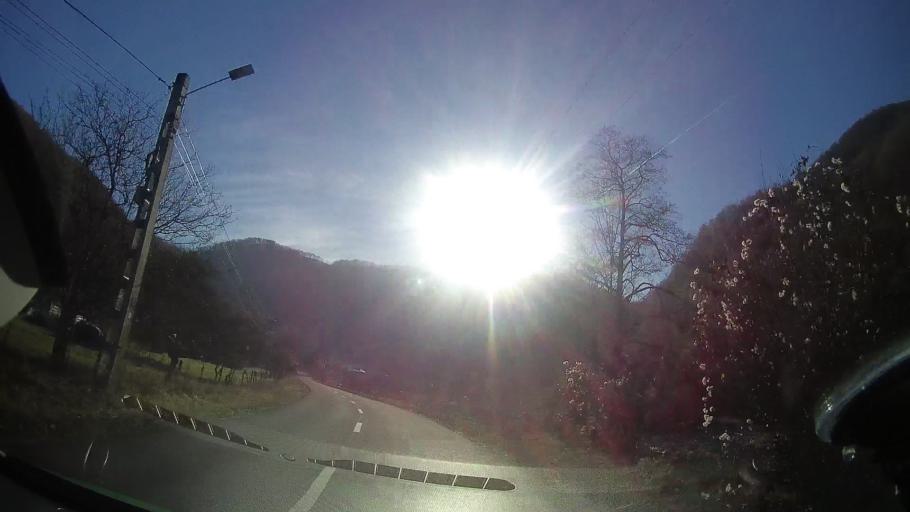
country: RO
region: Bihor
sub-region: Comuna Bulz
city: Bulz
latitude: 46.9197
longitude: 22.6544
